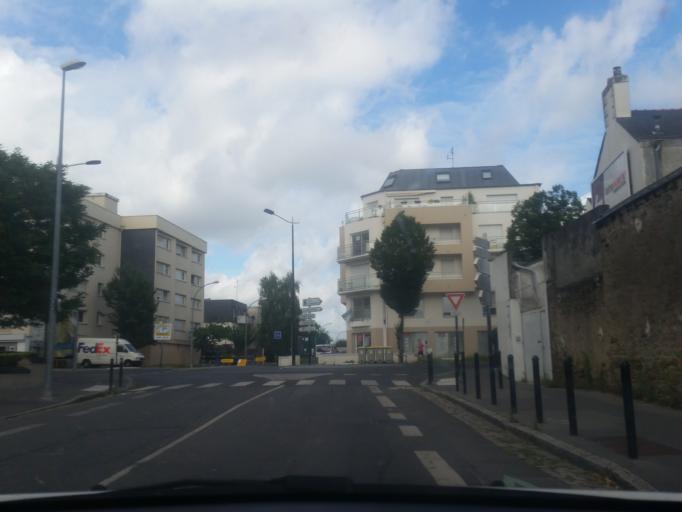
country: FR
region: Pays de la Loire
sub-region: Departement de la Loire-Atlantique
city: Nantes
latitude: 47.2405
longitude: -1.5299
